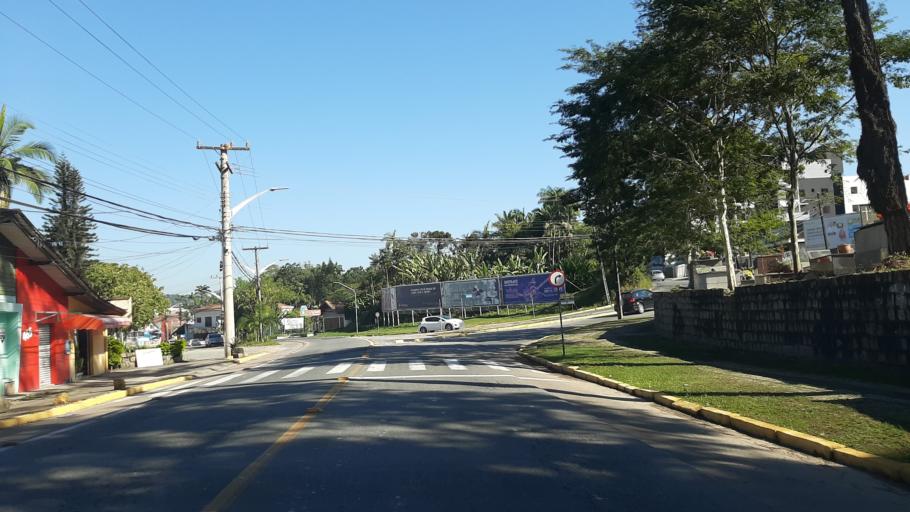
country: BR
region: Santa Catarina
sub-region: Joinville
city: Joinville
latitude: -26.3134
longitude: -48.8594
